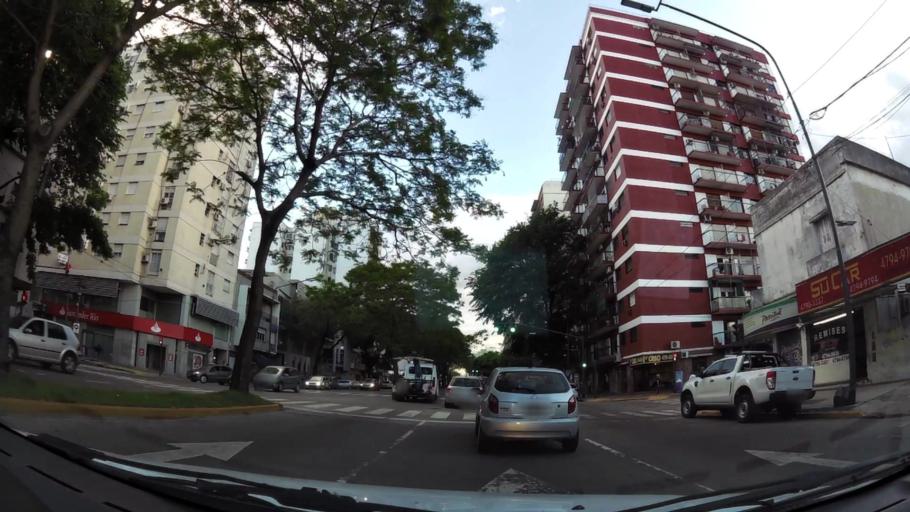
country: AR
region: Buenos Aires
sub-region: Partido de Vicente Lopez
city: Olivos
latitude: -34.5072
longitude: -58.4928
